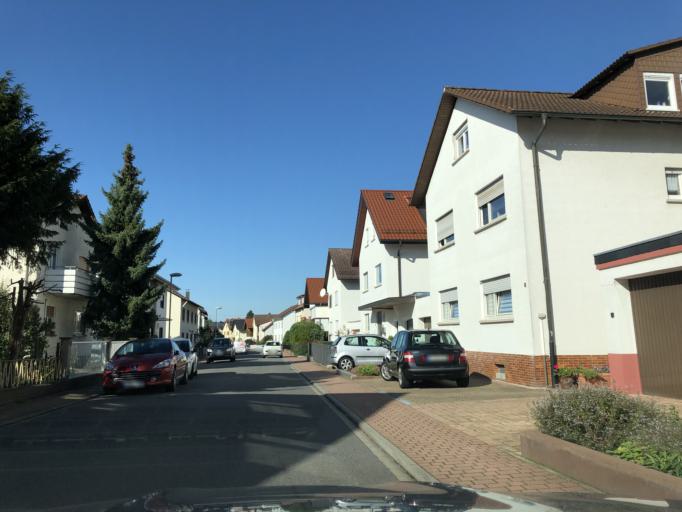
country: DE
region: Baden-Wuerttemberg
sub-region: Karlsruhe Region
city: Leimen
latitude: 49.3497
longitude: 8.6855
